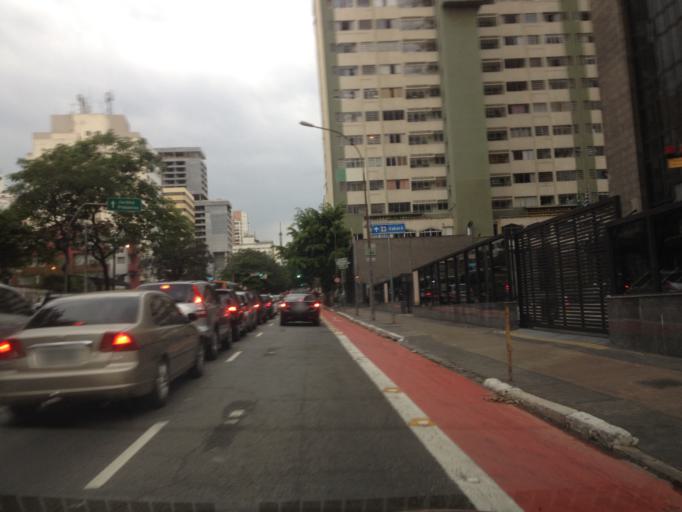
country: BR
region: Sao Paulo
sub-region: Sao Paulo
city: Sao Paulo
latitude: -23.5493
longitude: -46.6529
